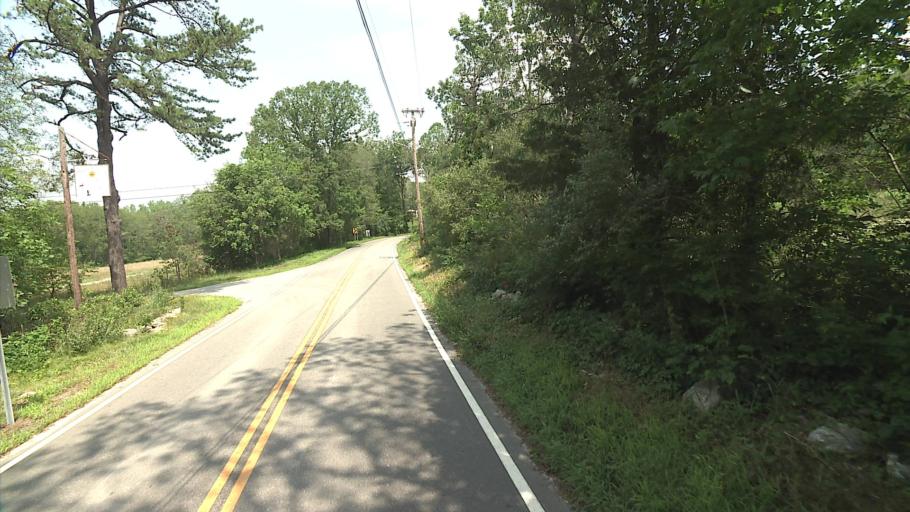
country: US
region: Connecticut
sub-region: Windham County
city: Danielson
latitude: 41.7637
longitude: -71.8473
